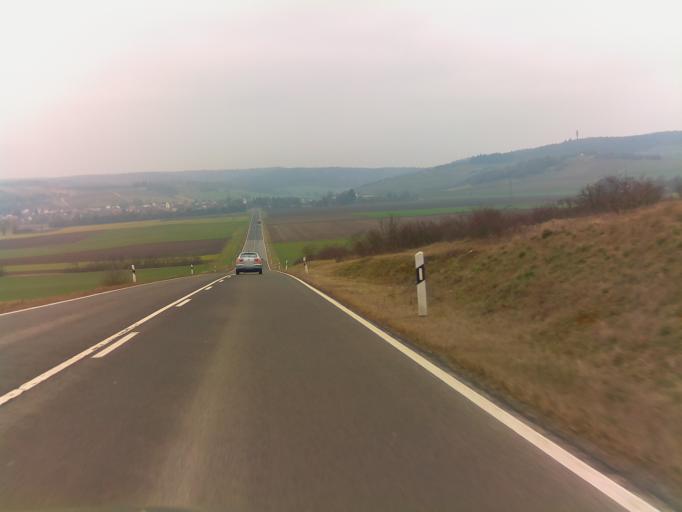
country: DE
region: Rheinland-Pfalz
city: Neu-Bamberg
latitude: 49.8073
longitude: 7.9254
